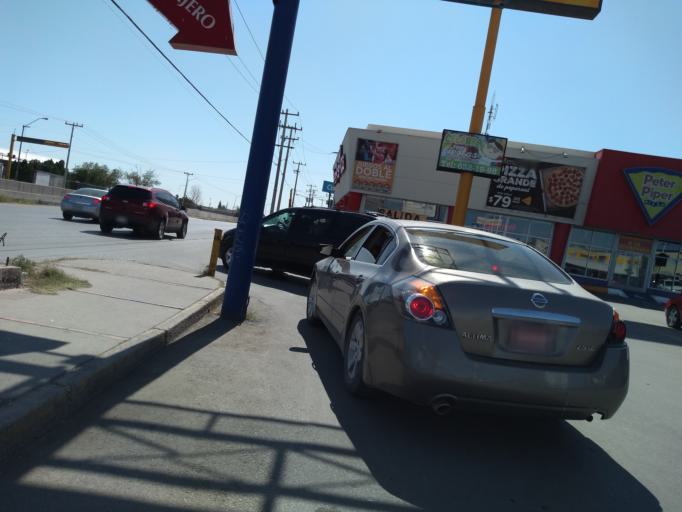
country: US
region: Texas
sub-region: El Paso County
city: El Paso
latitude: 31.7531
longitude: -106.4989
